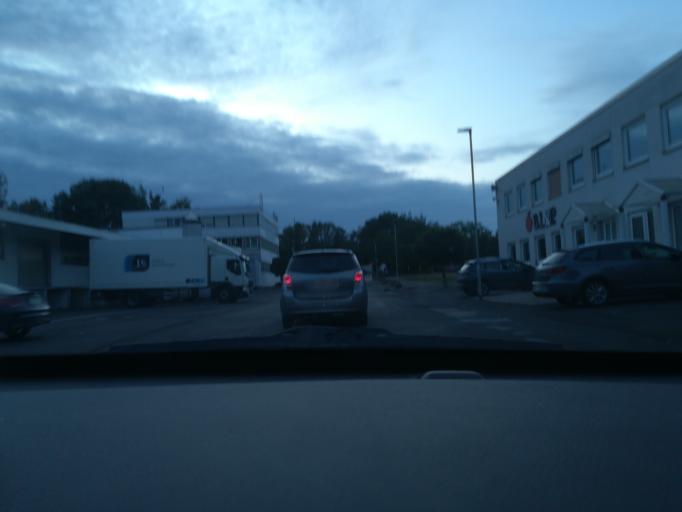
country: DE
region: Hesse
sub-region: Regierungsbezirk Kassel
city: Kassel
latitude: 51.3231
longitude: 9.4690
